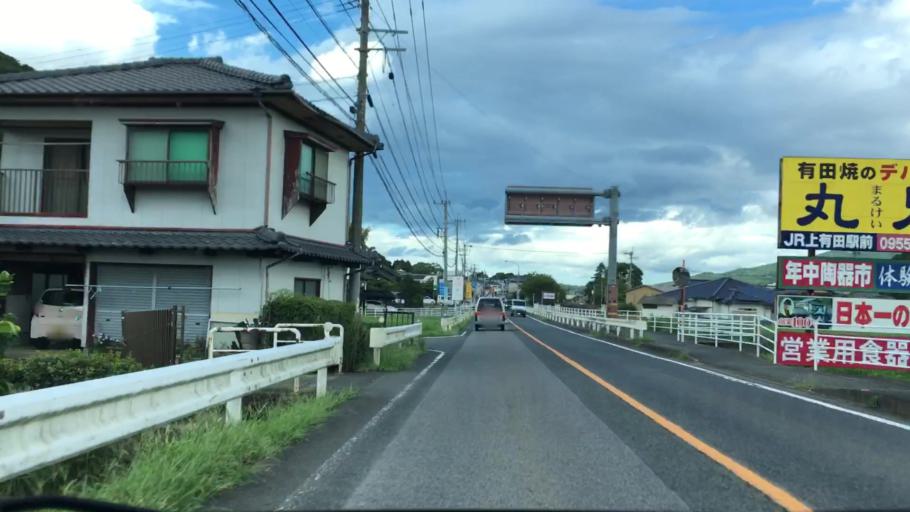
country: JP
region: Saga Prefecture
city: Imaricho-ko
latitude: 33.1991
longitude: 129.8504
